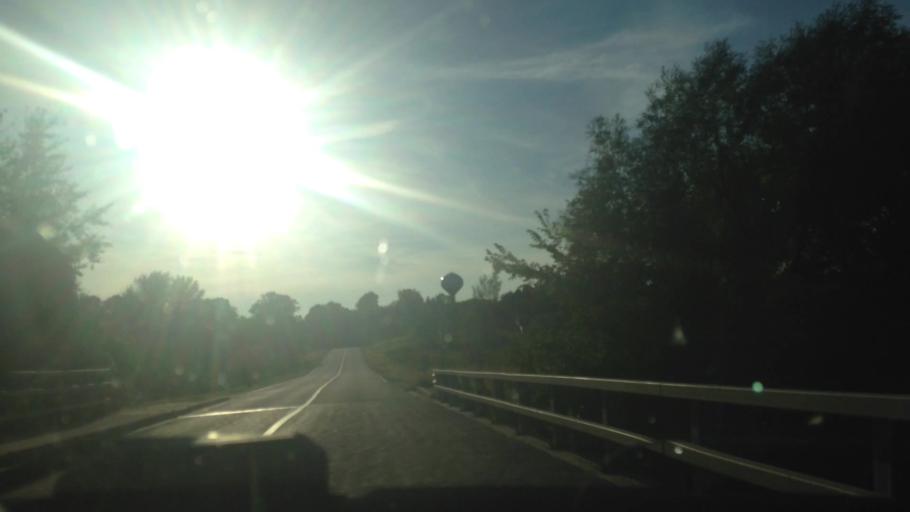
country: US
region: Wisconsin
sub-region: Dodge County
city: Mayville
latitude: 43.4934
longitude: -88.5308
